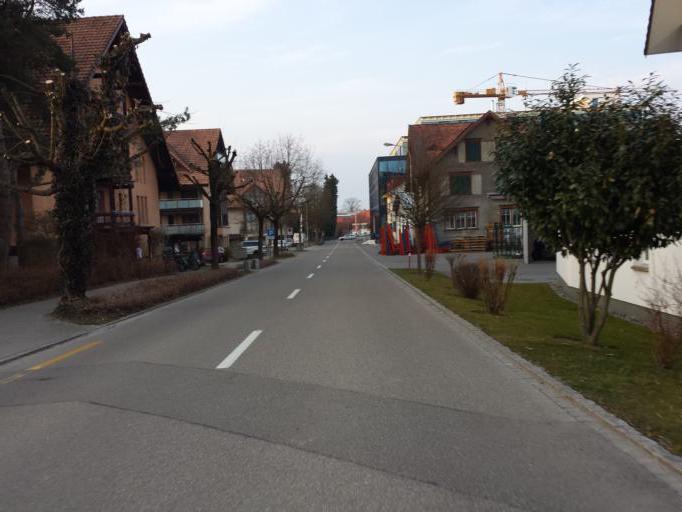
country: CH
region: Thurgau
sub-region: Arbon District
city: Egnach
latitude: 47.5432
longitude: 9.3806
